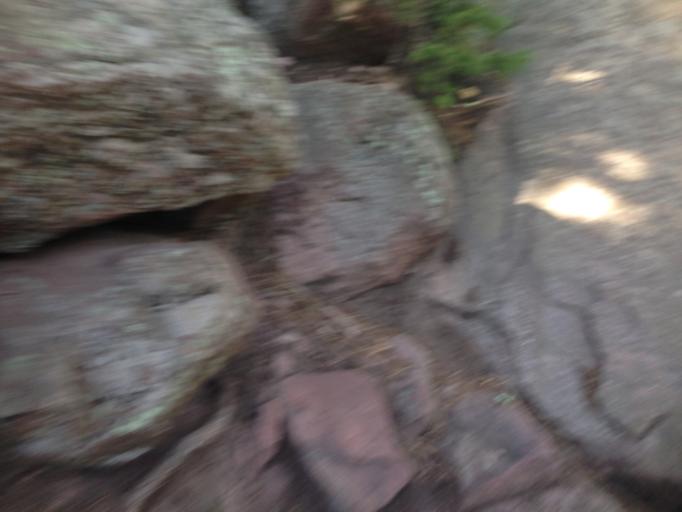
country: US
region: Colorado
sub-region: Boulder County
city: Boulder
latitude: 39.9896
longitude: -105.2904
